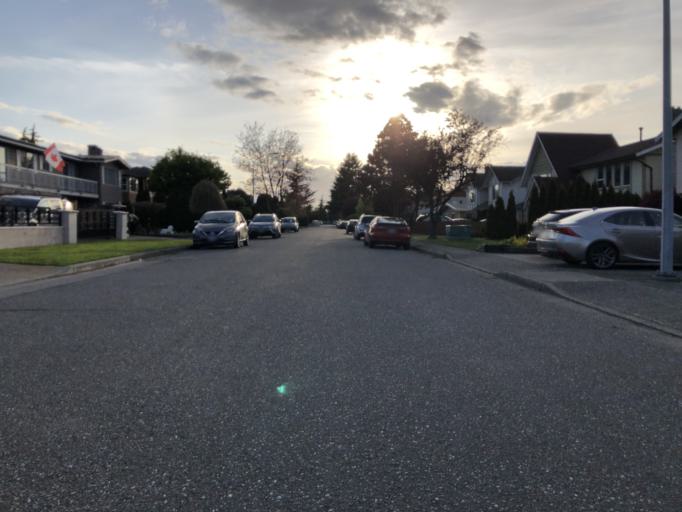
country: CA
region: British Columbia
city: Richmond
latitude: 49.1439
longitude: -123.1053
